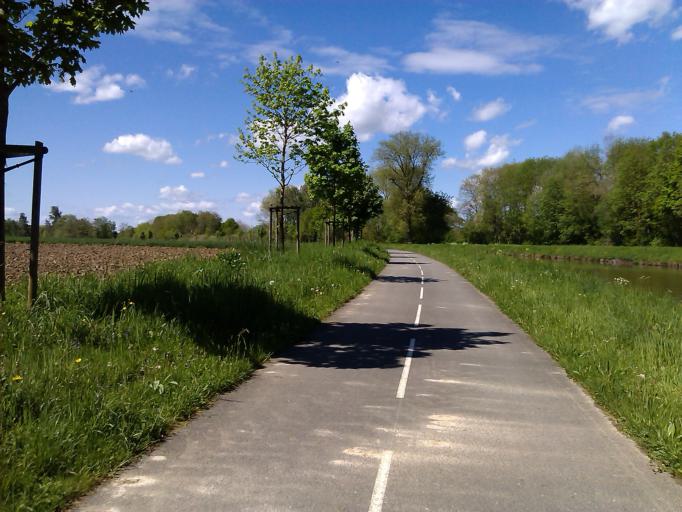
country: FR
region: Franche-Comte
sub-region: Territoire de Belfort
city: Montreux-Chateau
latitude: 47.5958
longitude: 6.9893
